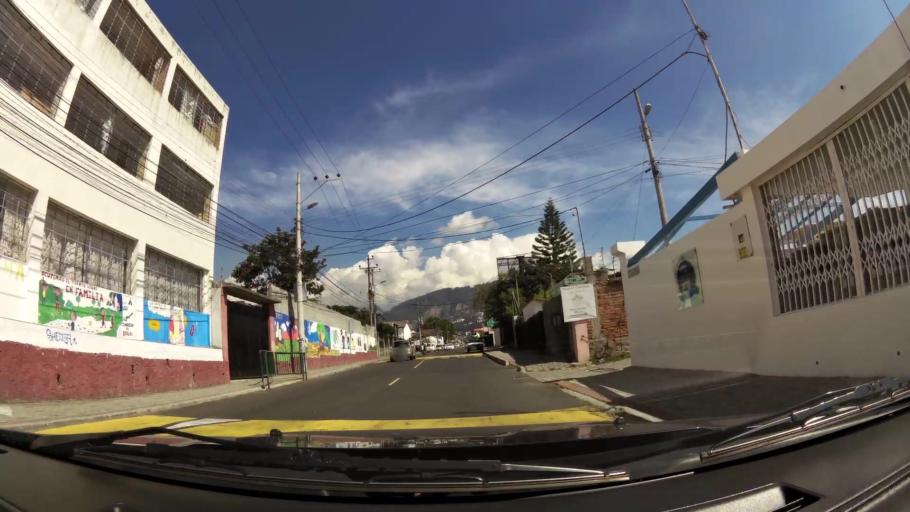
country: EC
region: Pichincha
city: Quito
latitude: -0.2016
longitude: -78.4274
